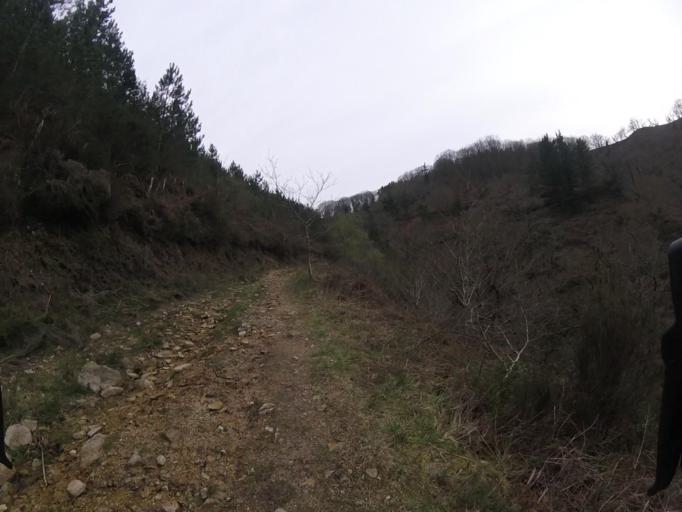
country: ES
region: Navarre
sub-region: Provincia de Navarra
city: Bera
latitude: 43.2927
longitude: -1.7356
